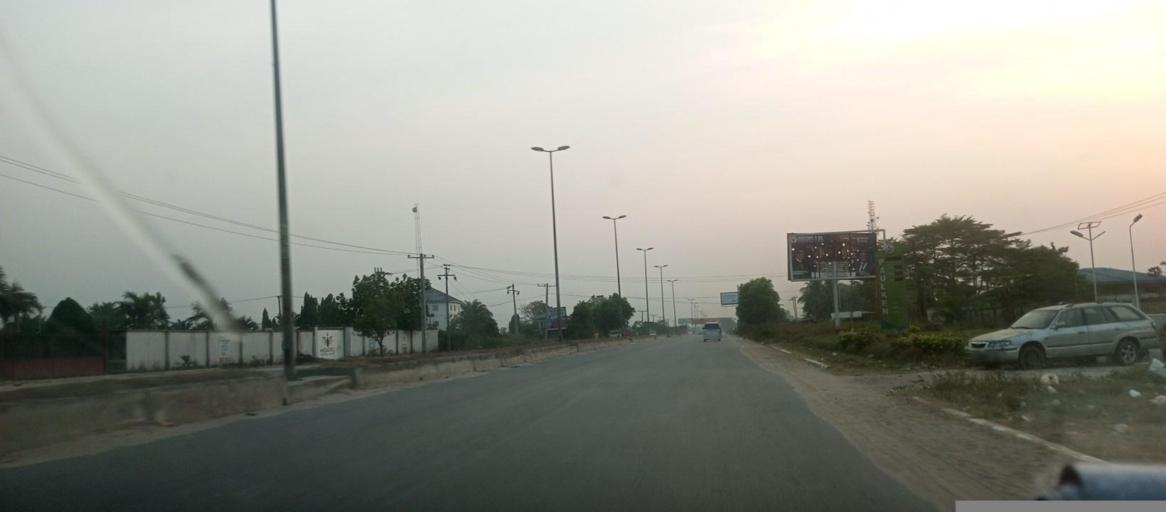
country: NG
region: Rivers
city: Emuoha
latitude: 4.9339
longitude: 7.0046
